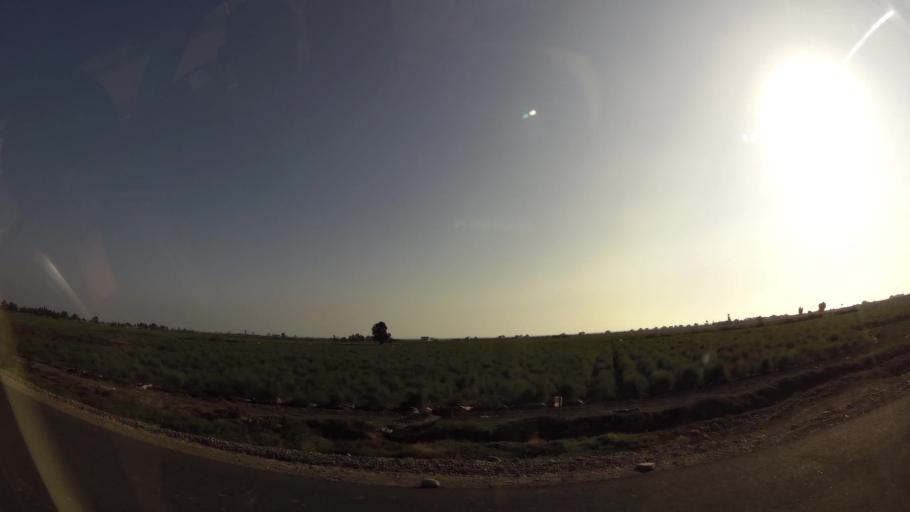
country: PE
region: Ica
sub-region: Provincia de Pisco
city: San Clemente
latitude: -13.5655
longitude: -76.1797
